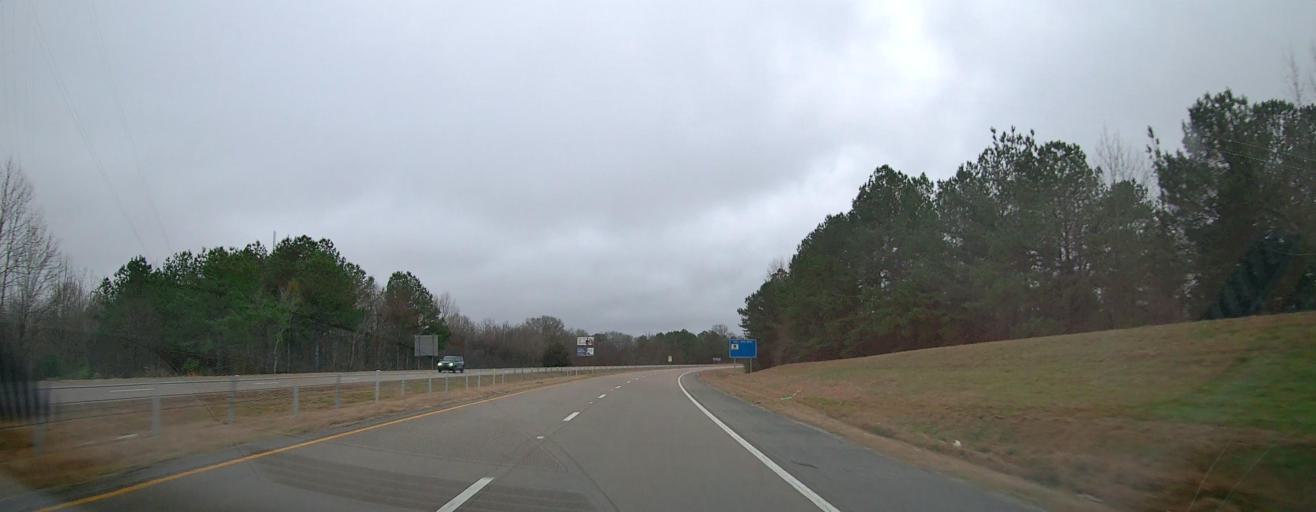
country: US
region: Mississippi
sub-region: Alcorn County
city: Corinth
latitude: 34.9211
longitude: -88.5428
